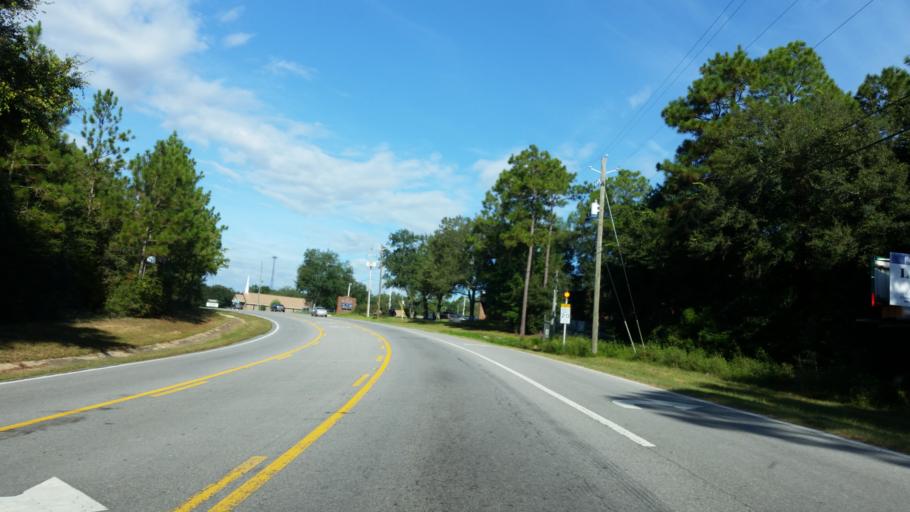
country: US
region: Florida
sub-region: Santa Rosa County
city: Milton
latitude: 30.6464
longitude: -87.0982
